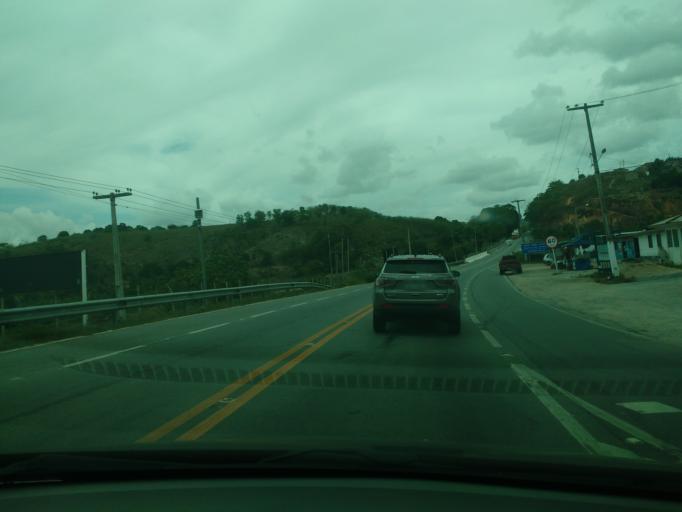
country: BR
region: Alagoas
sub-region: Uniao Dos Palmares
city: Uniao dos Palmares
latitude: -9.2414
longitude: -36.0121
